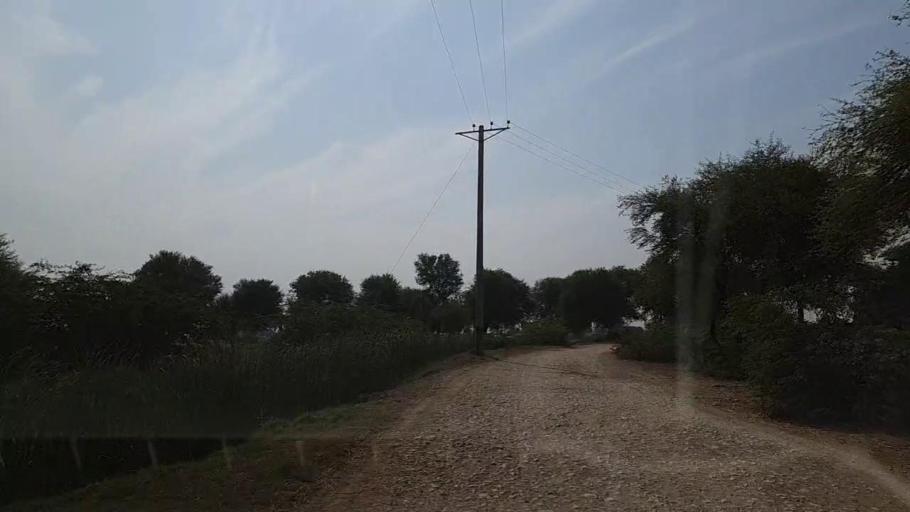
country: PK
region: Sindh
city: Mirpur Batoro
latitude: 24.6156
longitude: 68.2369
